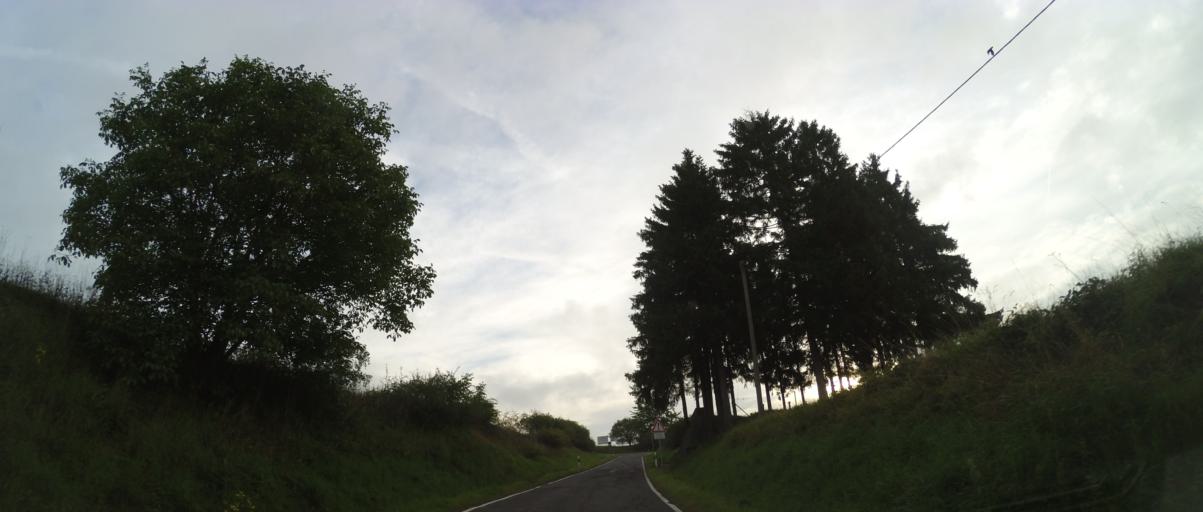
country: DE
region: Rheinland-Pfalz
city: Dreis-Bruck
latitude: 50.2765
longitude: 6.8131
